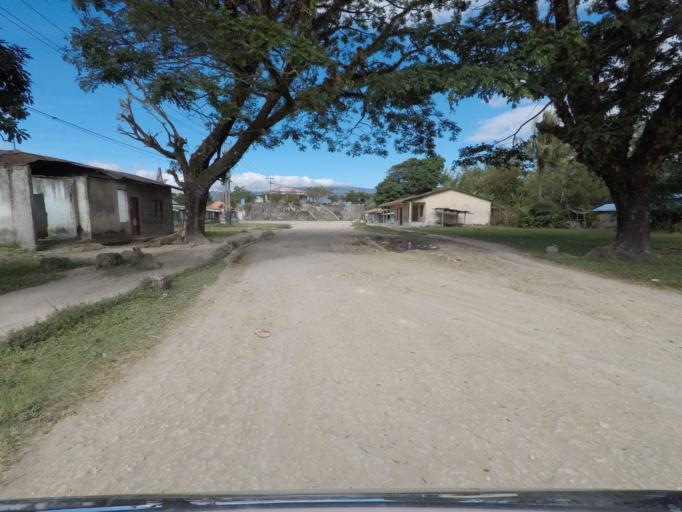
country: TL
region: Baucau
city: Venilale
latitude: -8.6431
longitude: 126.3788
